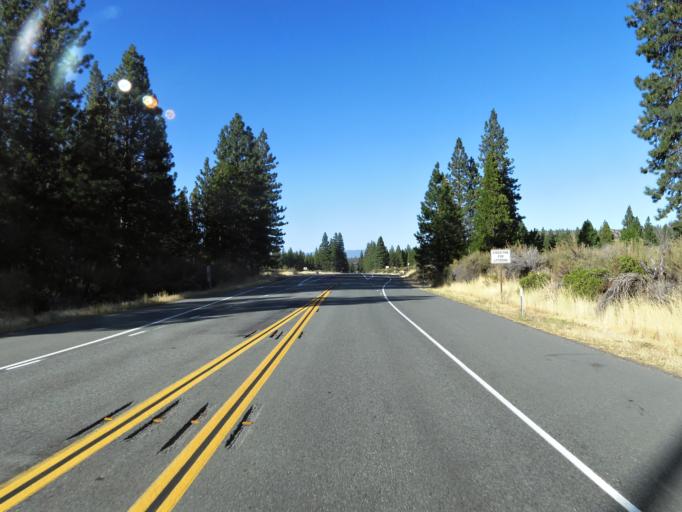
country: US
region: California
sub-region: Siskiyou County
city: Weed
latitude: 41.4520
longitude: -122.3613
